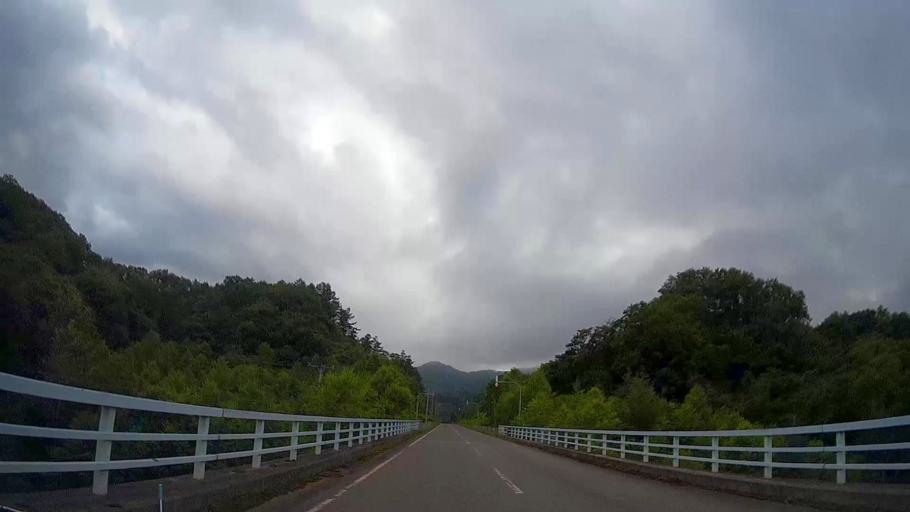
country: JP
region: Hokkaido
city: Nanae
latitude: 42.0726
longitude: 140.5155
